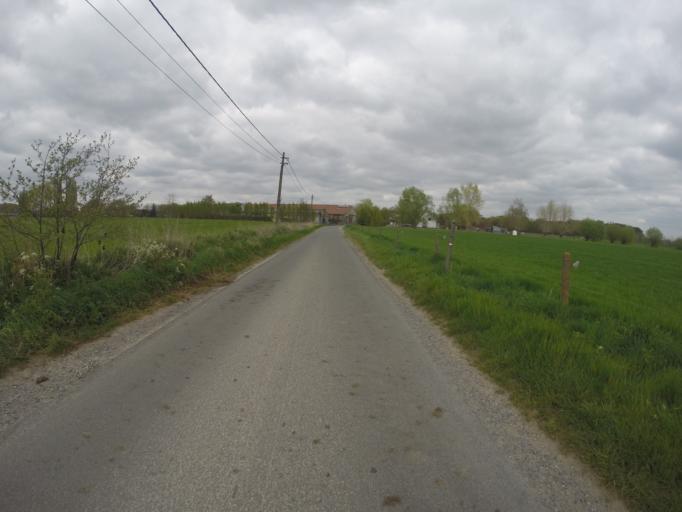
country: BE
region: Flanders
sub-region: Provincie Oost-Vlaanderen
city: Aalter
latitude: 51.0364
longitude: 3.4479
